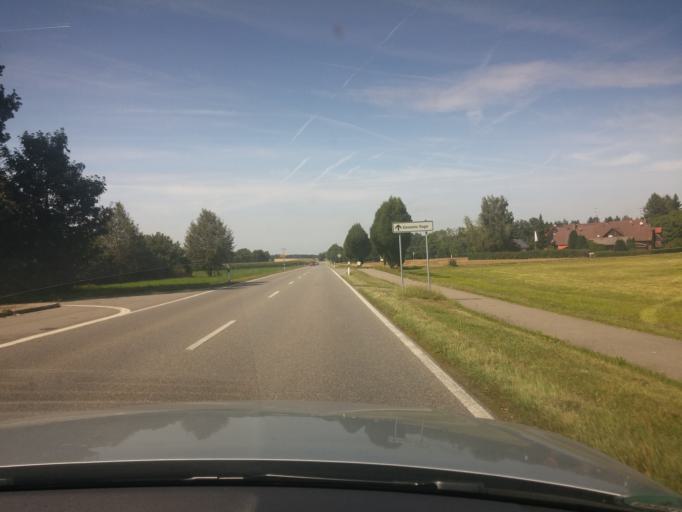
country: DE
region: Baden-Wuerttemberg
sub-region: Tuebingen Region
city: Bad Schussenried
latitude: 48.0316
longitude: 9.6395
